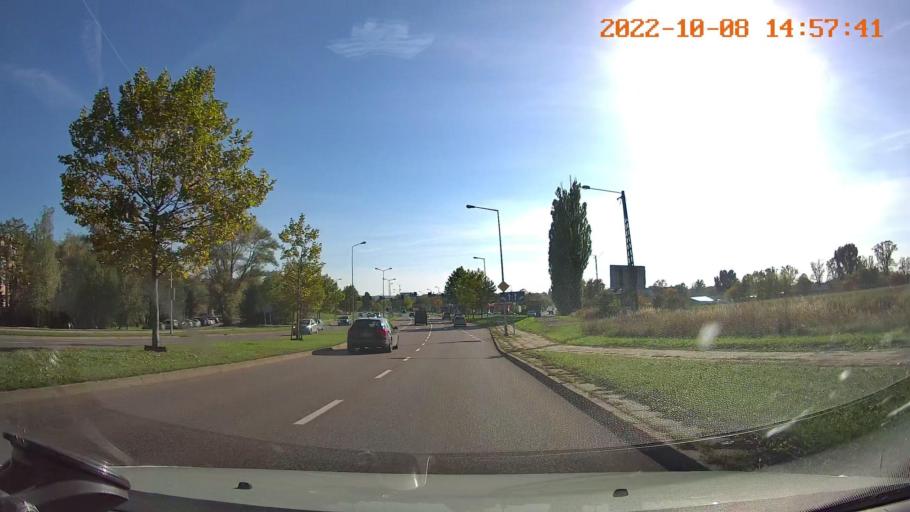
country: PL
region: Lesser Poland Voivodeship
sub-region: Powiat tarnowski
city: Tarnow
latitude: 50.0294
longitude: 20.9984
